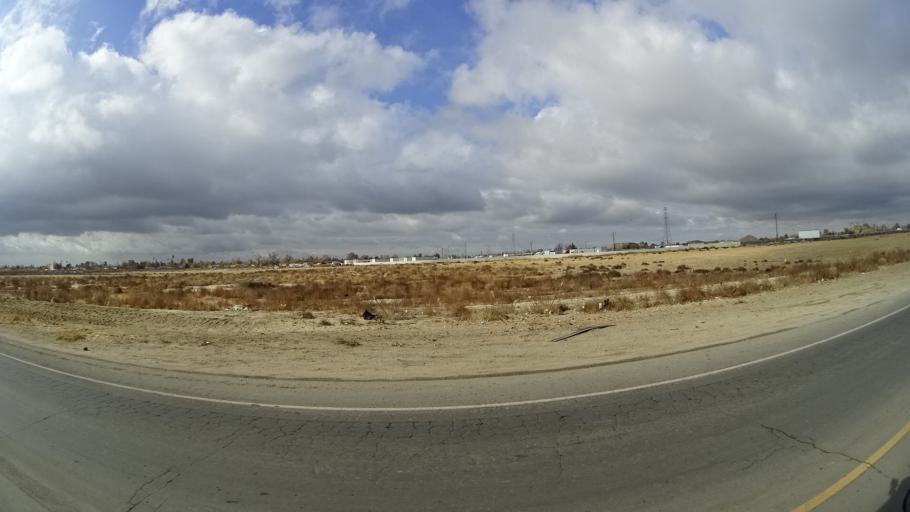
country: US
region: California
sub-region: Kern County
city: Greenfield
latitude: 35.3119
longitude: -118.9854
